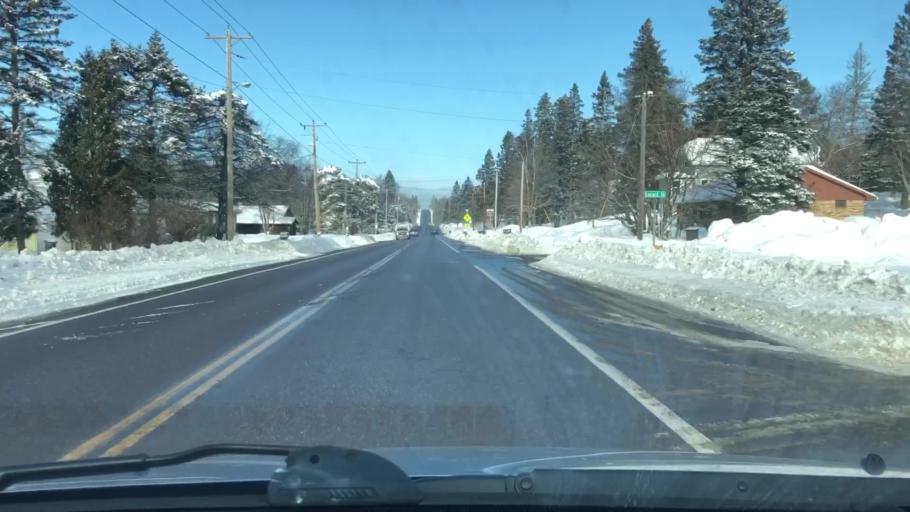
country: US
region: Minnesota
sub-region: Saint Louis County
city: Duluth
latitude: 46.8028
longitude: -92.1322
